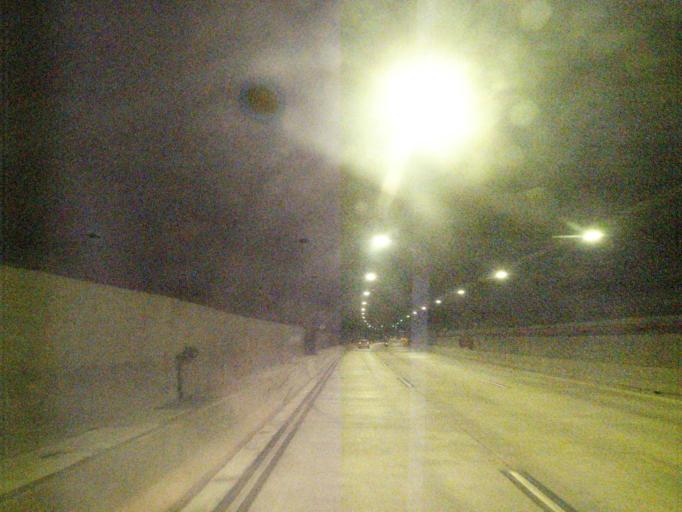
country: BR
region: Rio de Janeiro
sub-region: Rio De Janeiro
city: Rio de Janeiro
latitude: -22.8970
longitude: -43.1792
